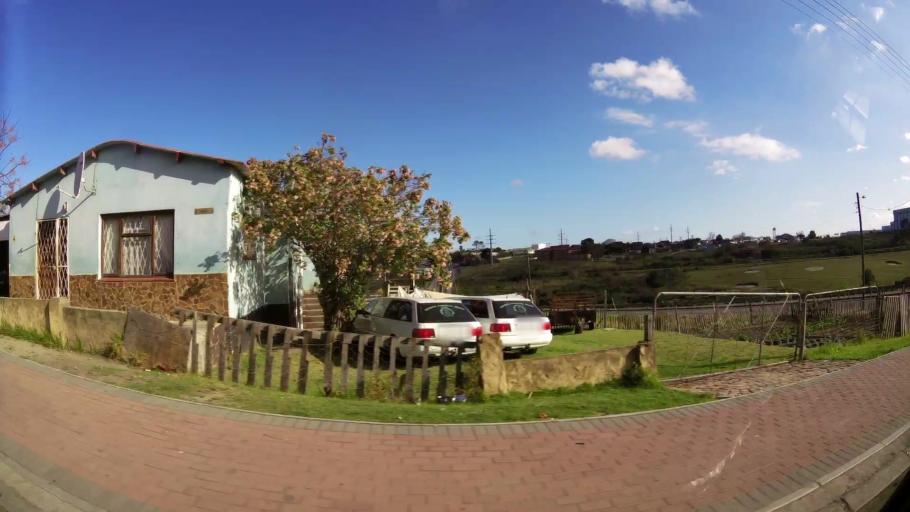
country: ZA
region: Western Cape
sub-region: Eden District Municipality
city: George
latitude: -33.9785
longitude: 22.4775
